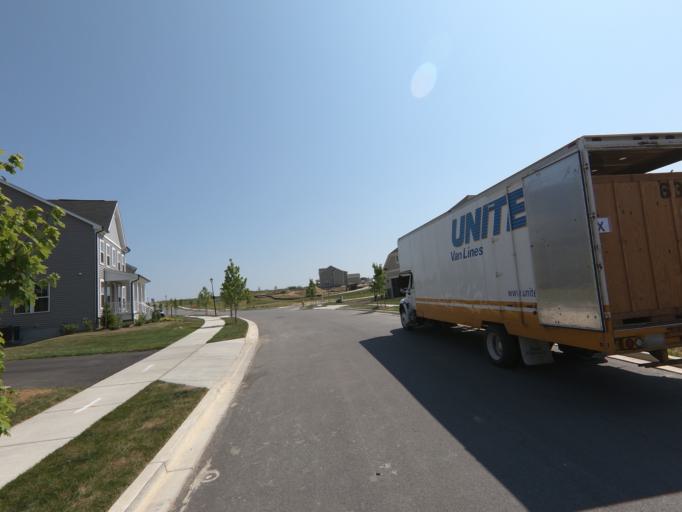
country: US
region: Maryland
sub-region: Frederick County
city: Bartonsville
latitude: 39.3841
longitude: -77.3727
